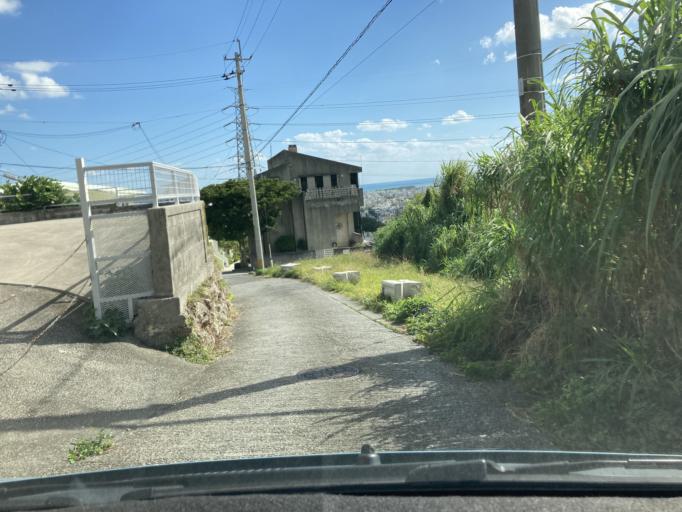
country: JP
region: Okinawa
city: Okinawa
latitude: 26.3269
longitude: 127.8180
